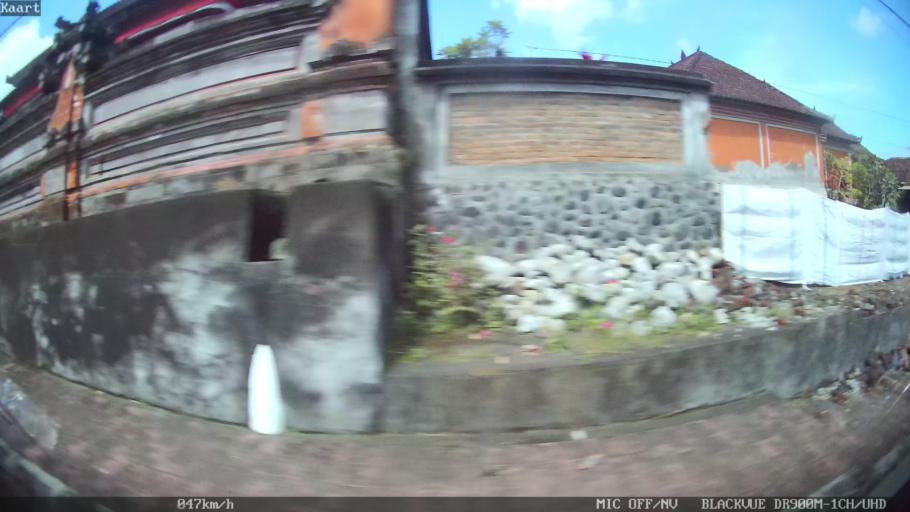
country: ID
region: Bali
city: Banjar Kelodan
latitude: -8.5303
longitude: 115.3288
